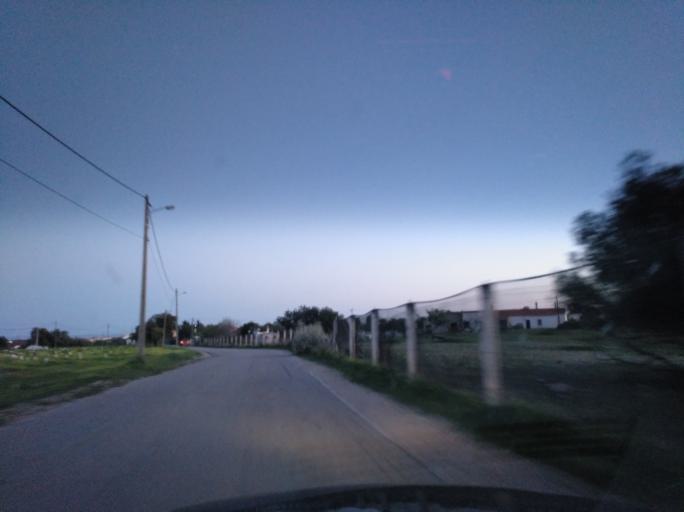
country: PT
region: Faro
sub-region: Vila Real de Santo Antonio
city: Monte Gordo
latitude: 37.1866
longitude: -7.5090
